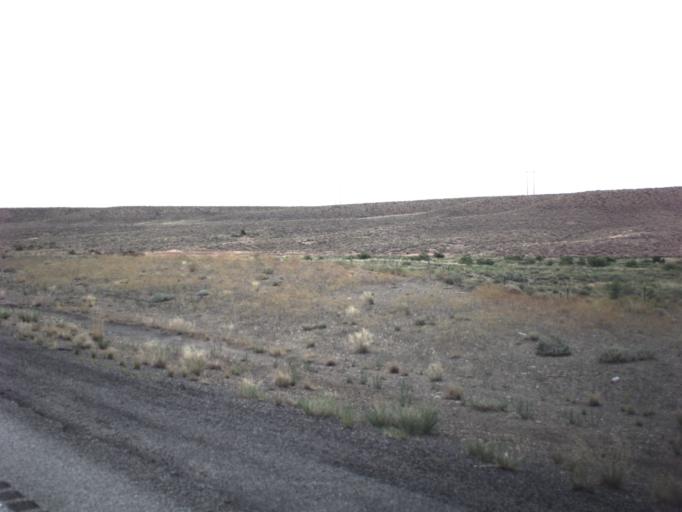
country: US
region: Utah
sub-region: Carbon County
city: Wellington
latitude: 39.5425
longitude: -110.6125
